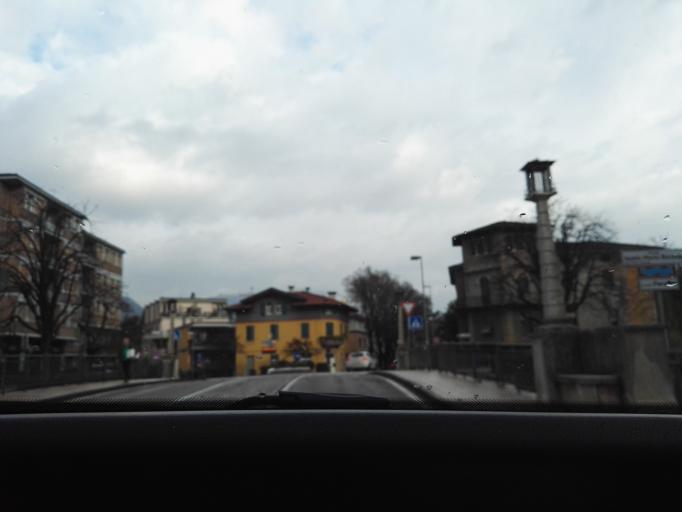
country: IT
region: Trentino-Alto Adige
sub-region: Provincia di Trento
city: Trento
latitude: 46.0624
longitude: 11.1326
